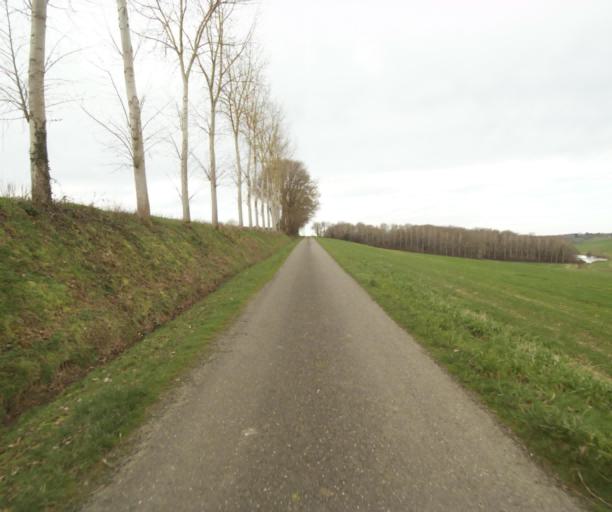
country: FR
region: Aquitaine
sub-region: Departement des Landes
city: Gabarret
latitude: 43.9254
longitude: -0.0005
